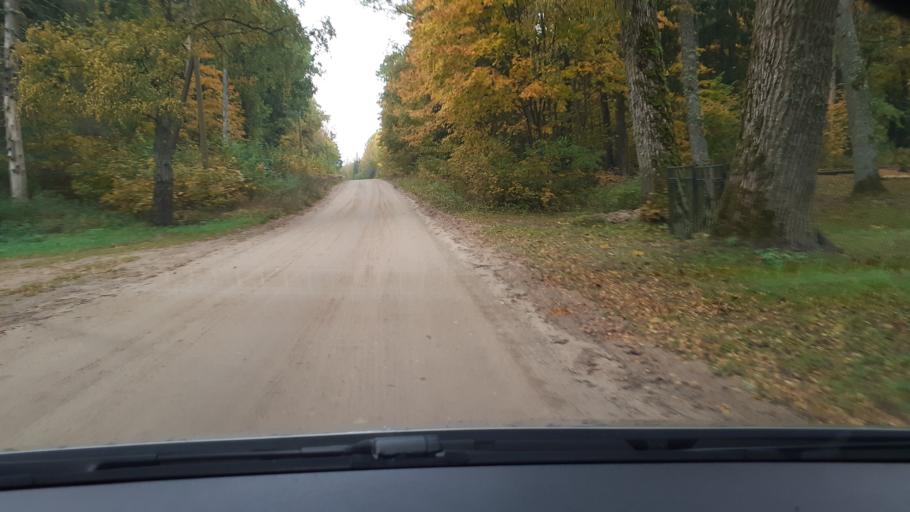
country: LV
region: Kuldigas Rajons
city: Kuldiga
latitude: 57.0303
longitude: 21.9152
